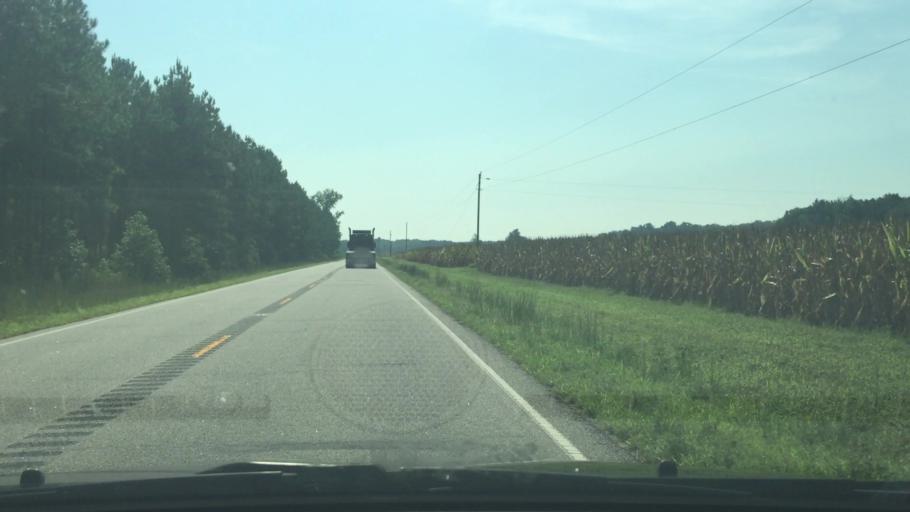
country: US
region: Virginia
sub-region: Sussex County
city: Sussex
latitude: 36.9809
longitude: -77.2360
